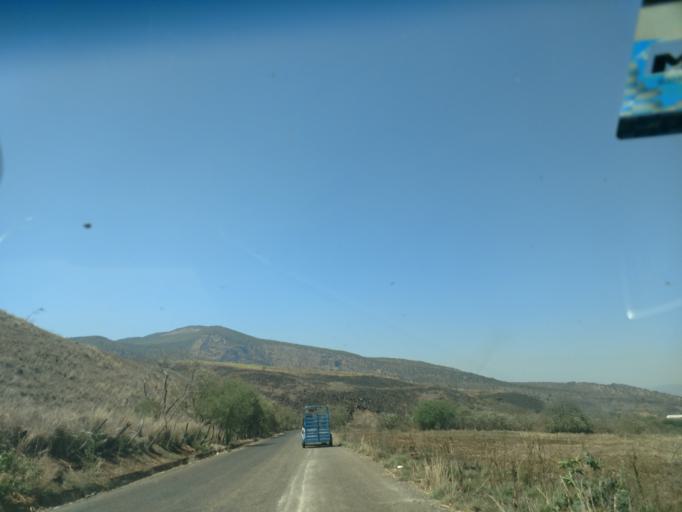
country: MX
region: Nayarit
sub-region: Tepic
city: La Corregidora
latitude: 21.5026
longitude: -104.7321
